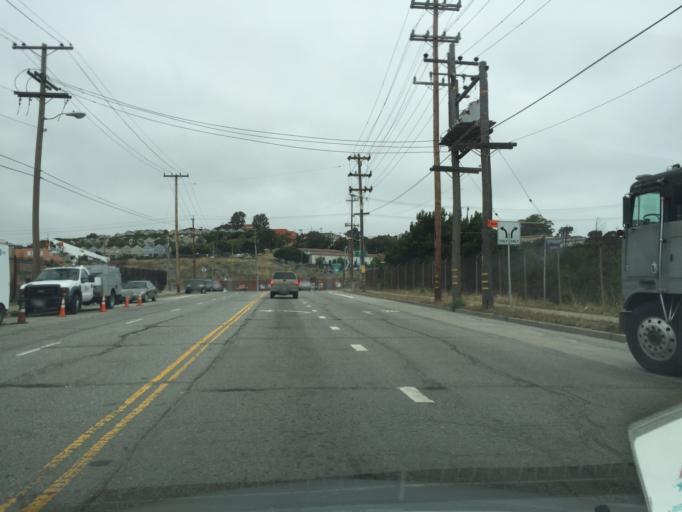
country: US
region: California
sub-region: San Francisco County
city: San Francisco
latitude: 37.7486
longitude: -122.3968
